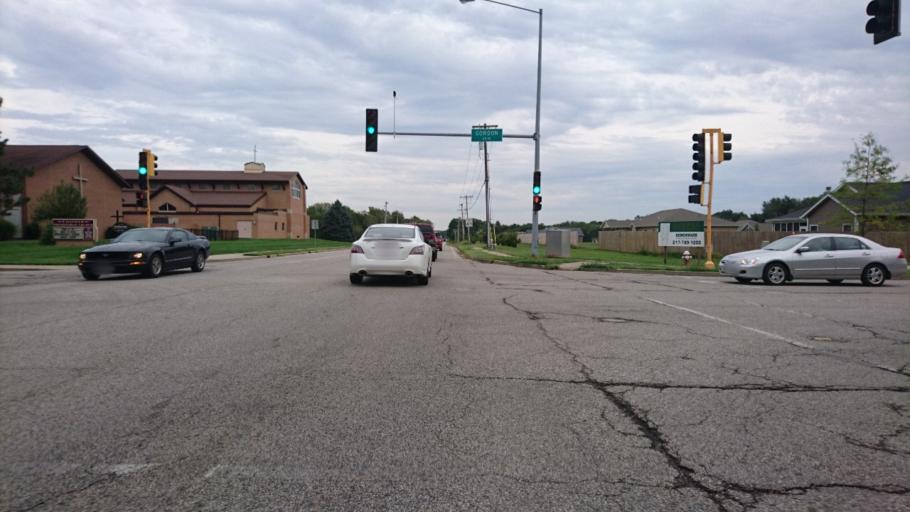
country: US
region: Illinois
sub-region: Sangamon County
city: Chatham
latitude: 39.6768
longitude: -89.6816
